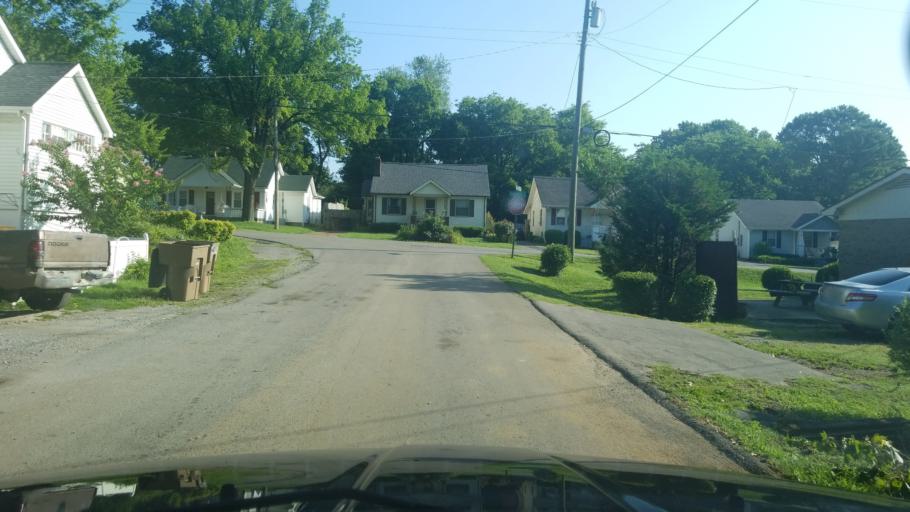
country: US
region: Tennessee
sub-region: Davidson County
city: Oak Hill
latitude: 36.1046
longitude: -86.7386
